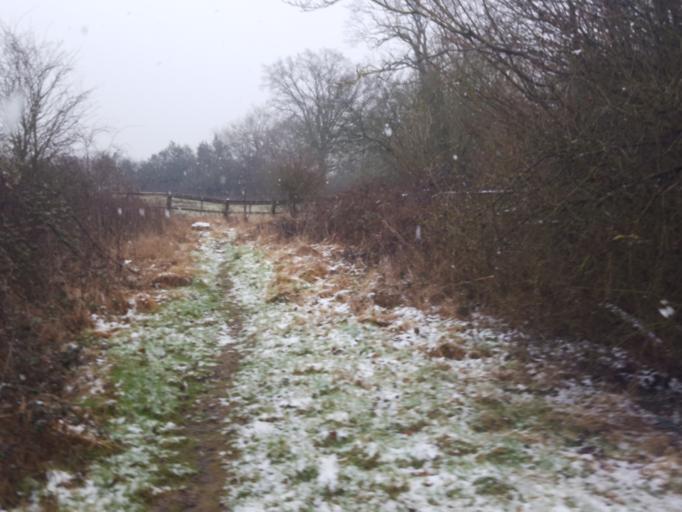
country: GB
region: England
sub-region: West Sussex
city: Gossops Green
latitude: 51.1240
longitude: -0.2365
